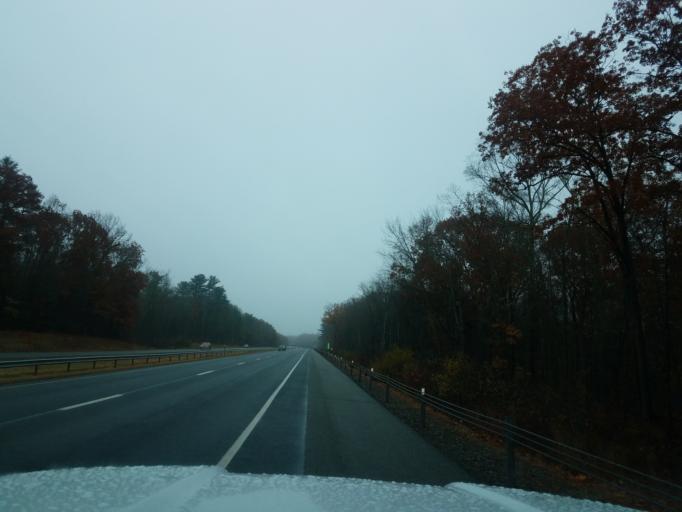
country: US
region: Connecticut
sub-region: Windham County
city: Danielson
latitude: 41.7779
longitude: -71.8722
